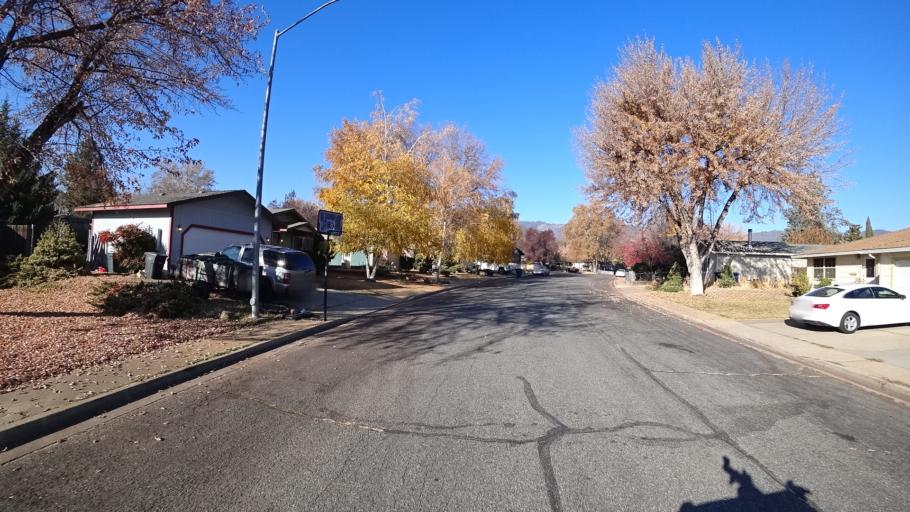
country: US
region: California
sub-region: Siskiyou County
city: Yreka
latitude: 41.7217
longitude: -122.6455
